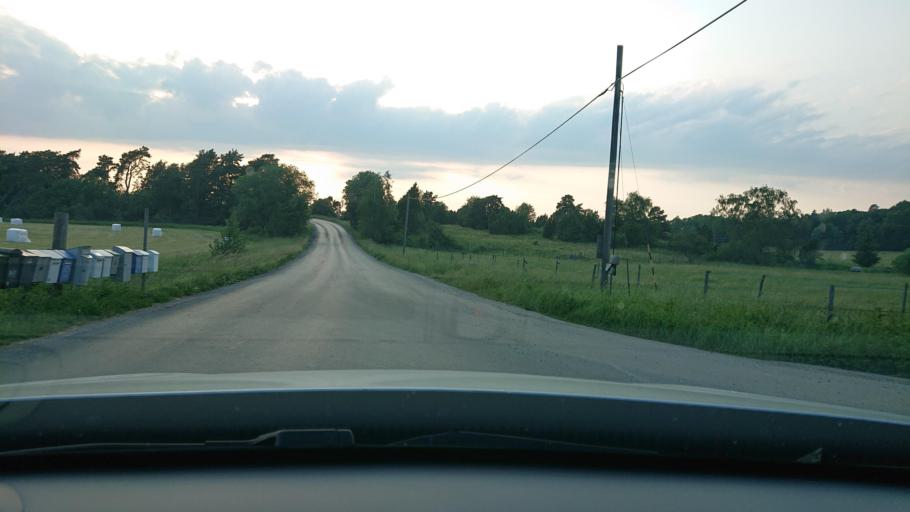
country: SE
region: Stockholm
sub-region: Osterakers Kommun
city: Akersberga
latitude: 59.5078
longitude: 18.3166
